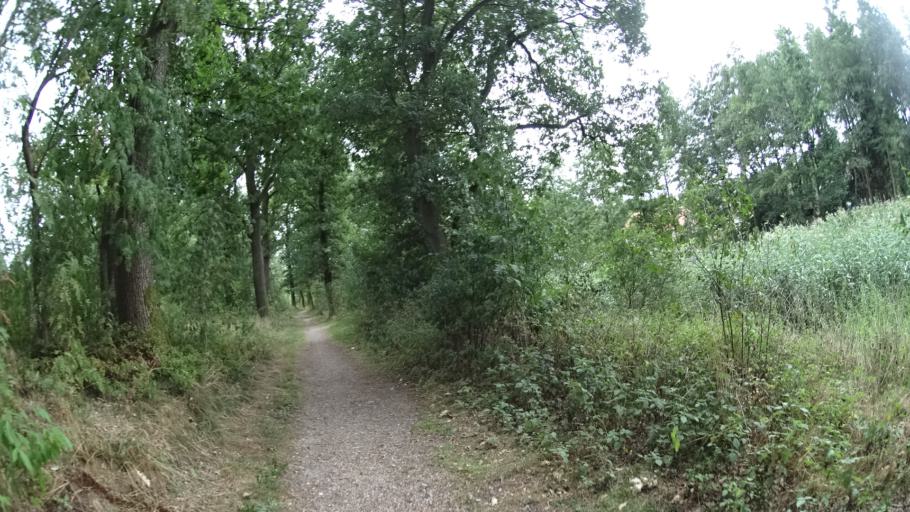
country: DE
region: Lower Saxony
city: Undeloh
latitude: 53.1936
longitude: 9.9790
